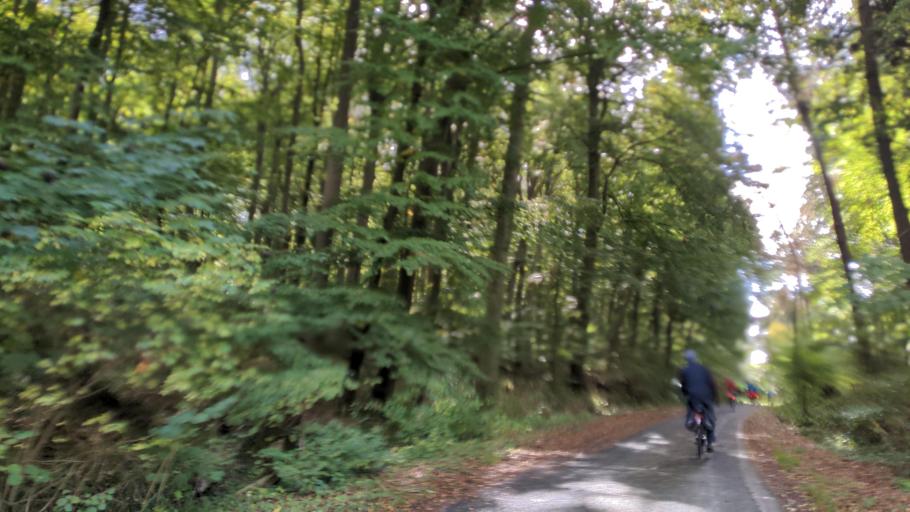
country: DE
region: Schleswig-Holstein
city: Buchholz
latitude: 53.7418
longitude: 10.7648
